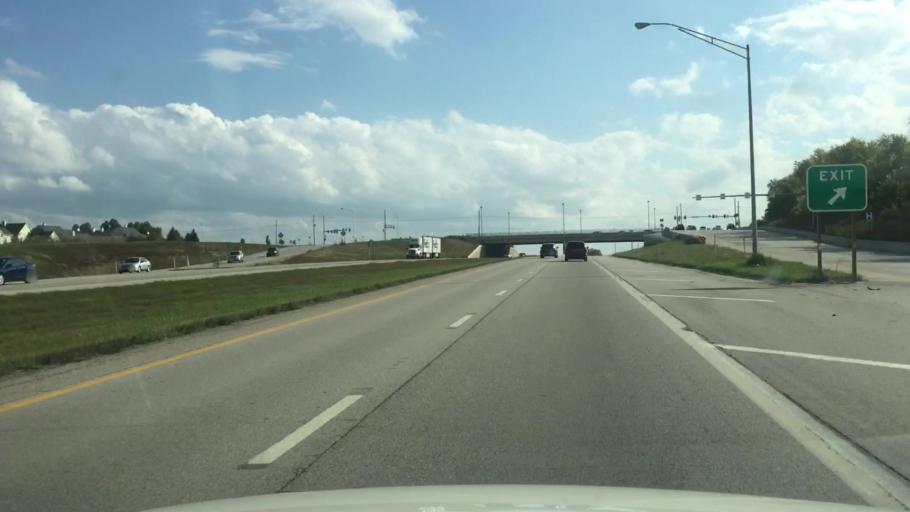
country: US
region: Kansas
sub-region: Johnson County
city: Lenexa
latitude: 38.8428
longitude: -94.6767
